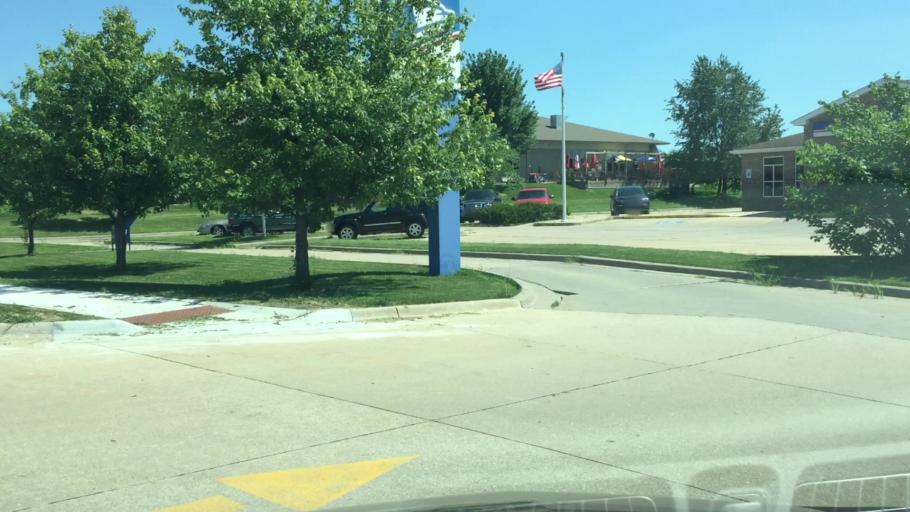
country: US
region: Iowa
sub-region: Johnson County
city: Solon
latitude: 41.7979
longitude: -91.4906
